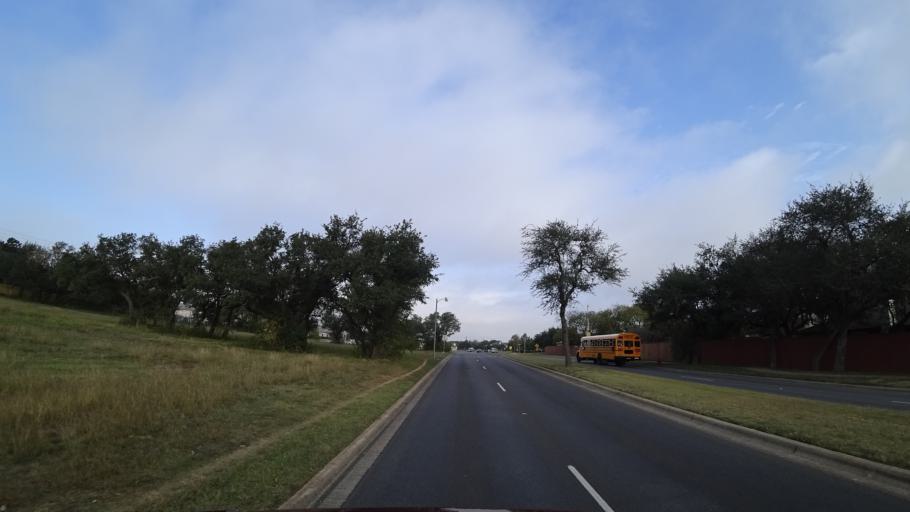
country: US
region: Texas
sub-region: Williamson County
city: Cedar Park
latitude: 30.5200
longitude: -97.8535
